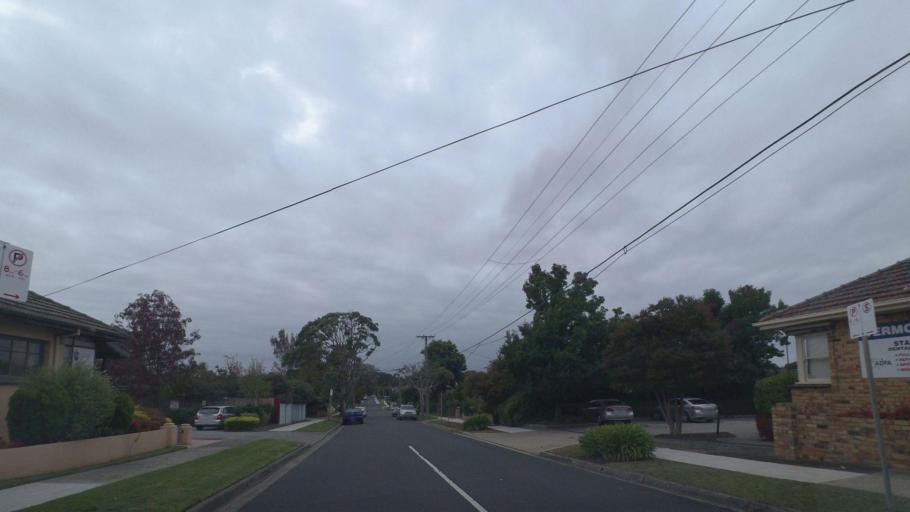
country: AU
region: Victoria
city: Forest Hill
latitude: -37.8360
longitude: 145.1848
